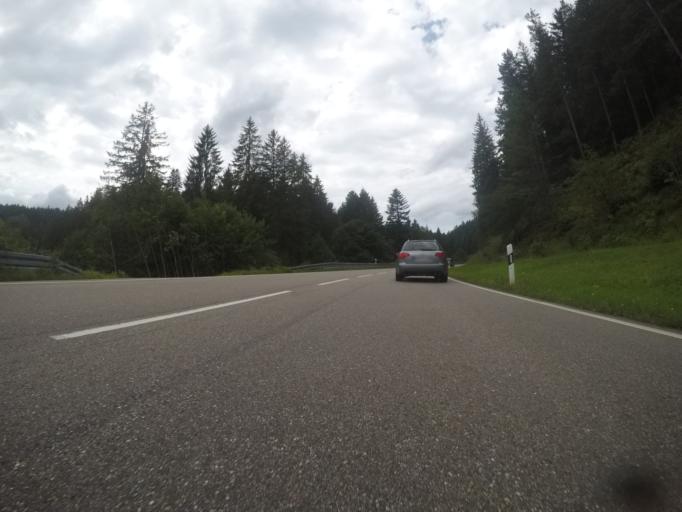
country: DE
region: Baden-Wuerttemberg
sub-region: Karlsruhe Region
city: Baiersbronn
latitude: 48.4601
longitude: 8.3526
